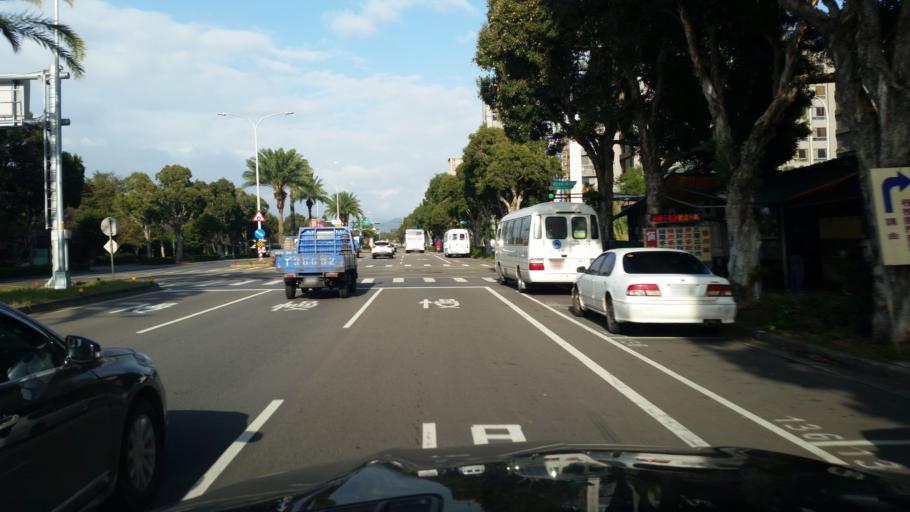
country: TW
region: Taiwan
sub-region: Taoyuan
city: Taoyuan
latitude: 25.0769
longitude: 121.3652
